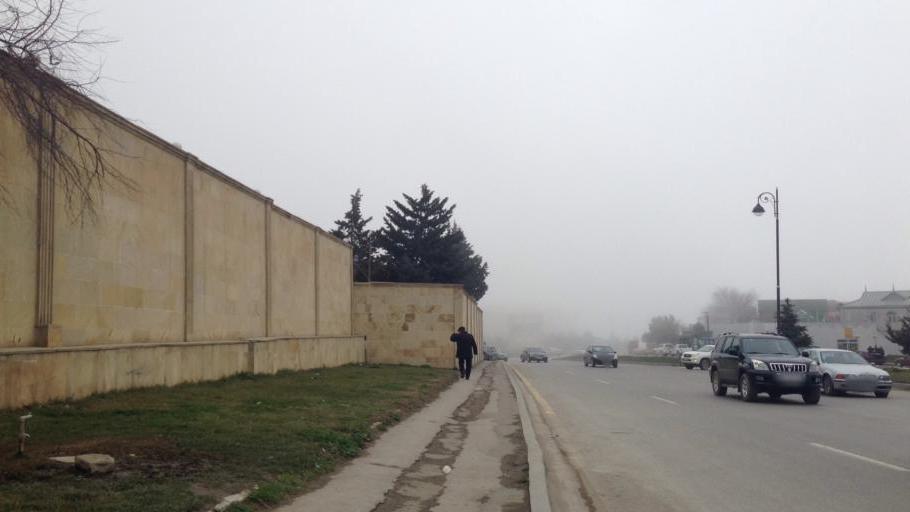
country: AZ
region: Baki
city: Qaracuxur
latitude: 40.3496
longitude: 49.9608
